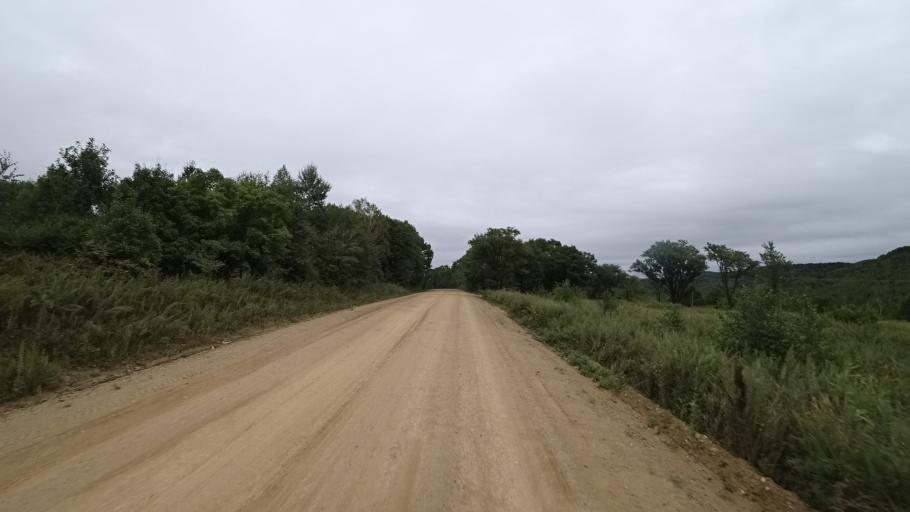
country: RU
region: Primorskiy
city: Rettikhovka
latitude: 44.1755
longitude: 132.8313
